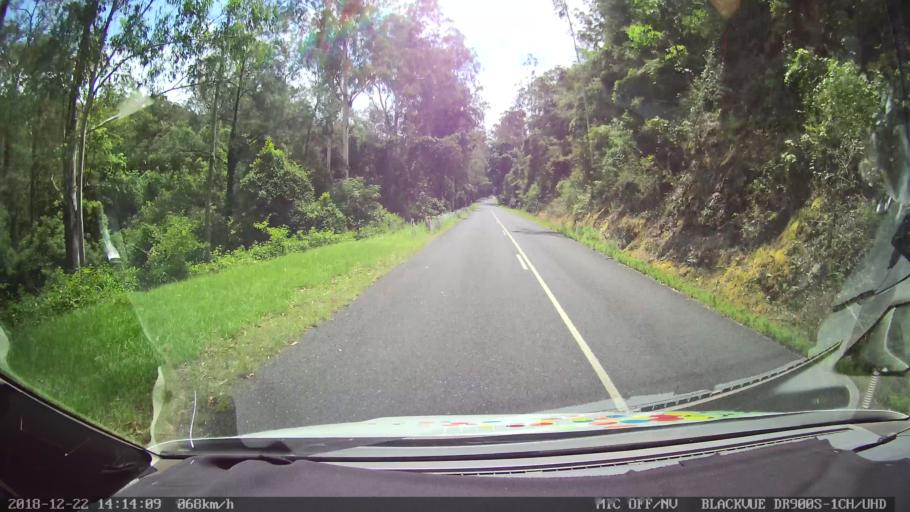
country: AU
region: New South Wales
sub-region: Clarence Valley
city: Coutts Crossing
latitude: -30.0010
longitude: 152.6913
